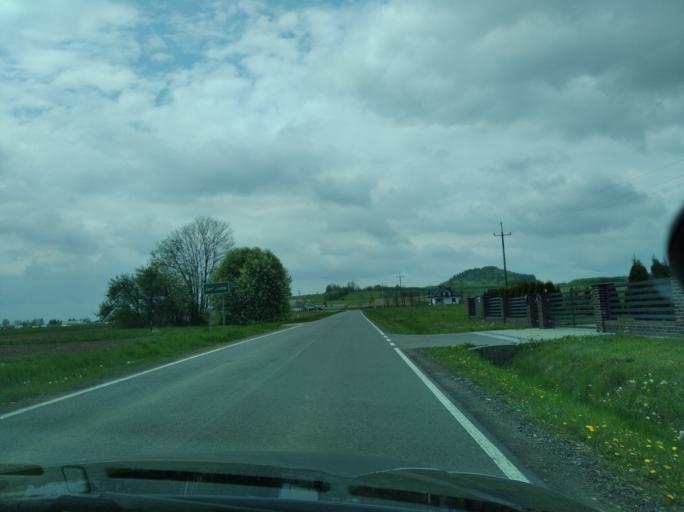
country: PL
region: Subcarpathian Voivodeship
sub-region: Powiat brzozowski
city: Jasionow
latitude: 49.6449
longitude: 21.9749
